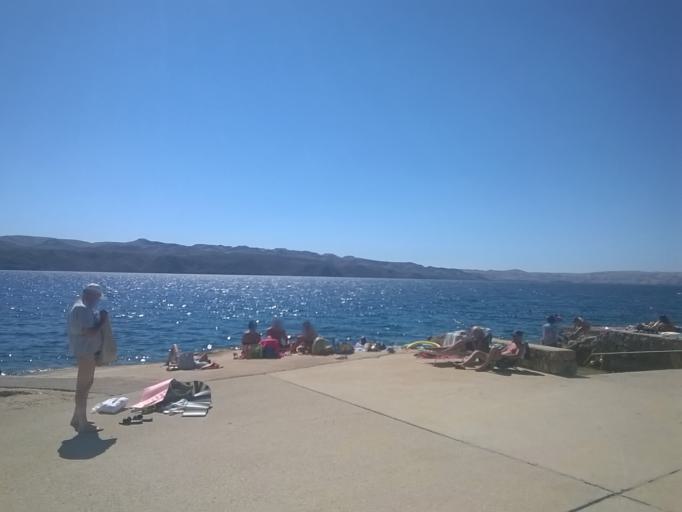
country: HR
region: Licko-Senjska
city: Karlobag
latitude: 44.5281
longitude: 15.0689
